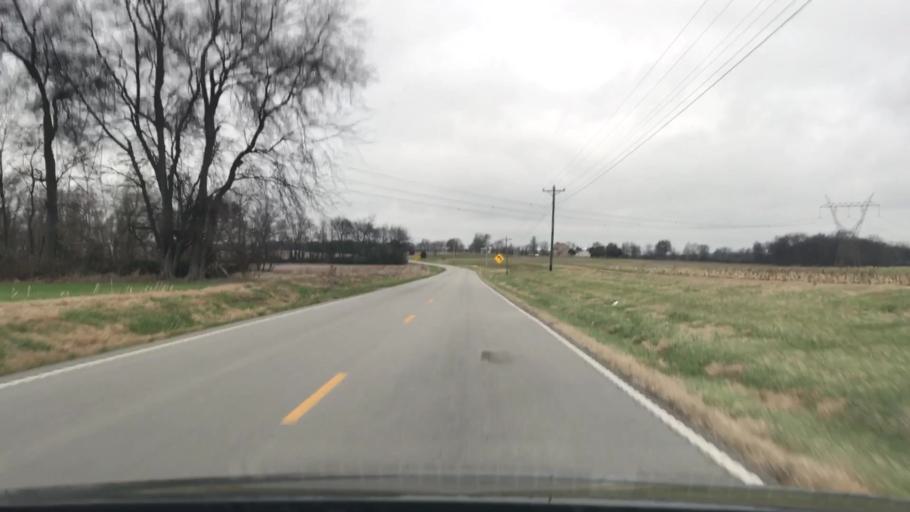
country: US
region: Kentucky
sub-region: Todd County
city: Guthrie
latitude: 36.6663
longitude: -87.1981
